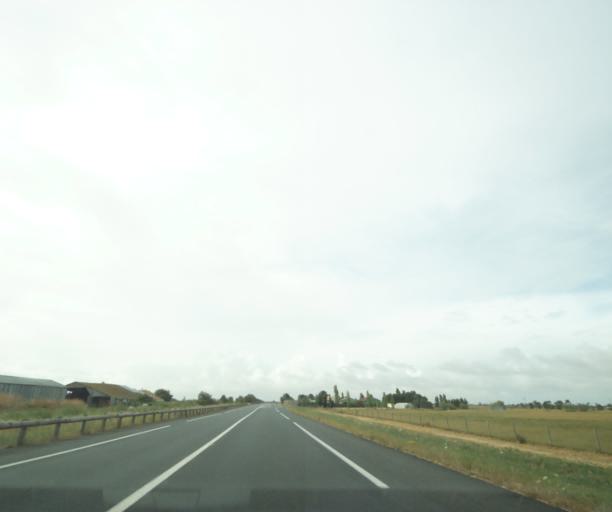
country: FR
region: Pays de la Loire
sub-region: Departement de la Vendee
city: Champagne-les-Marais
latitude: 46.4015
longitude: -1.0966
